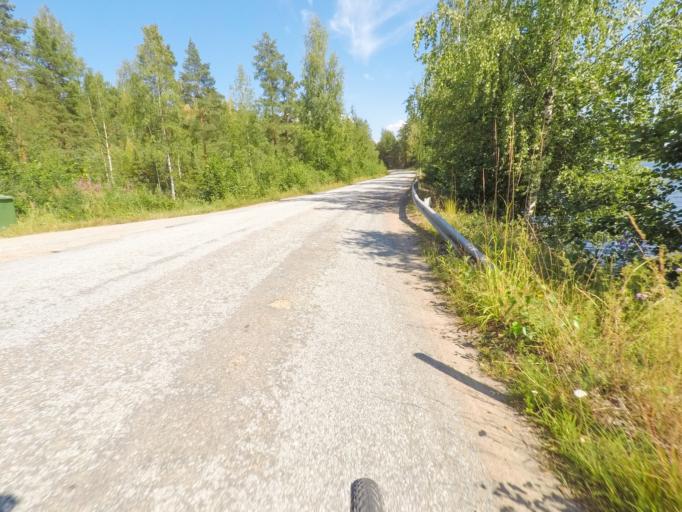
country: FI
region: Southern Savonia
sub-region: Mikkeli
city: Puumala
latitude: 61.4214
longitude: 28.0939
